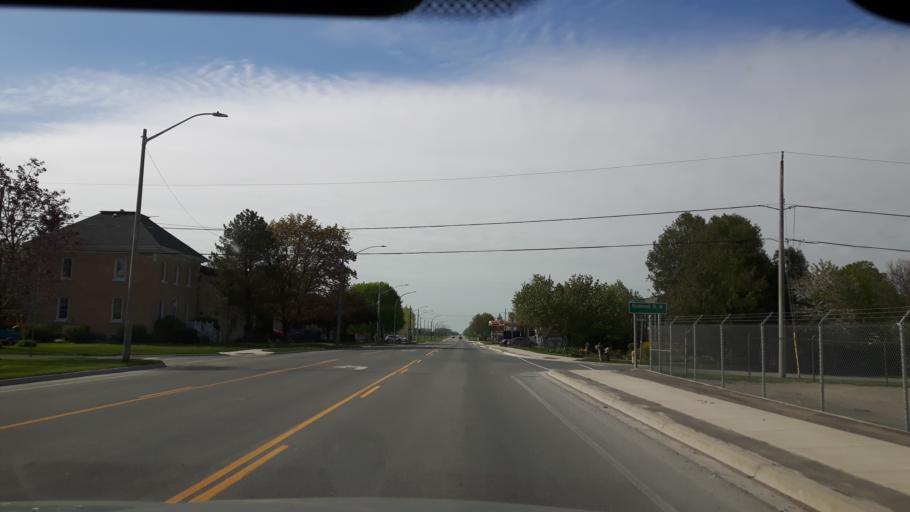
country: CA
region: Ontario
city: Bluewater
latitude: 43.4368
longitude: -81.4992
